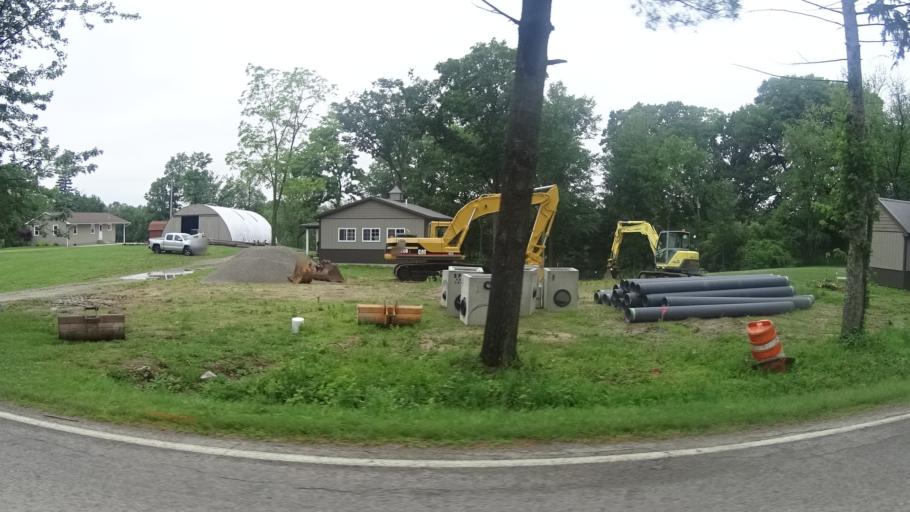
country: US
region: Ohio
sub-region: Erie County
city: Huron
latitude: 41.3458
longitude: -82.5564
